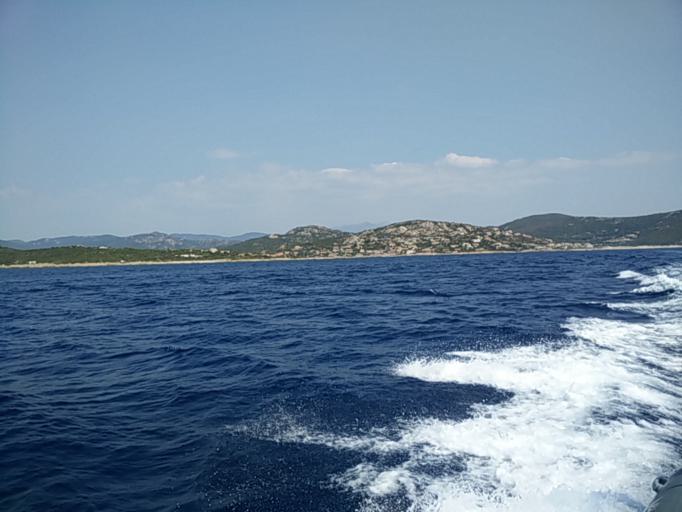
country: FR
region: Corsica
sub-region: Departement de la Corse-du-Sud
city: Propriano
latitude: 41.5383
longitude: 8.8373
